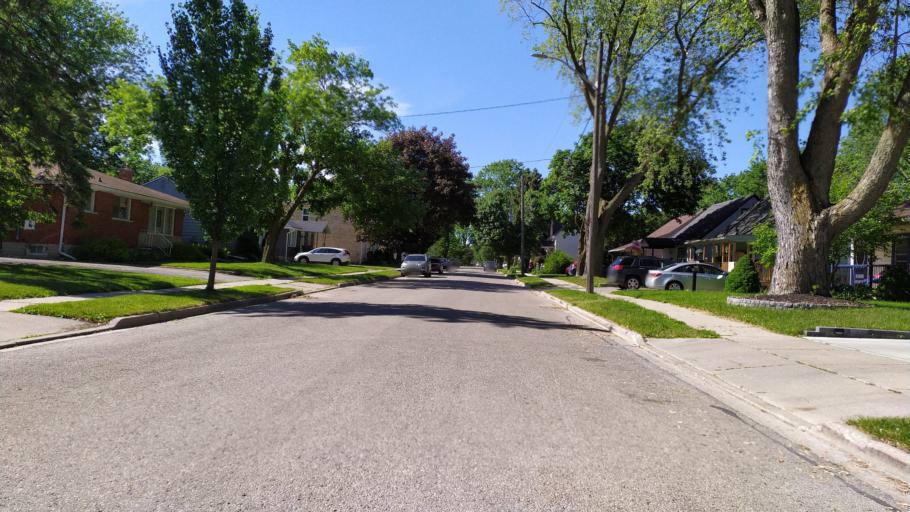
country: CA
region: Ontario
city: Stratford
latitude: 43.3595
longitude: -80.9828
